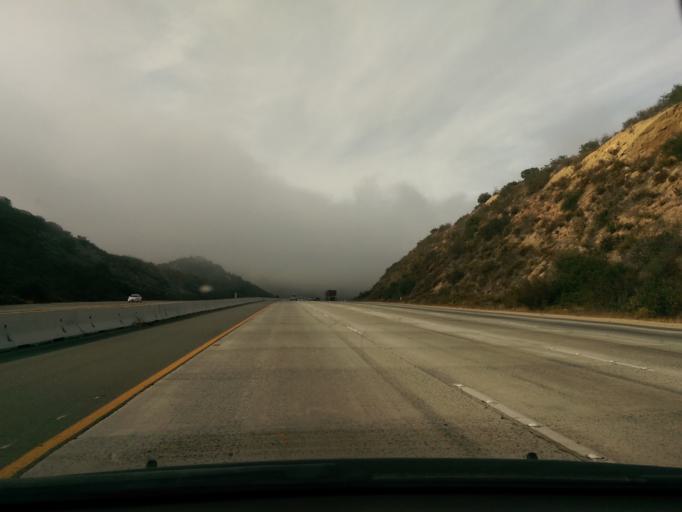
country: US
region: California
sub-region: Riverside County
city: Temecula
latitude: 33.4539
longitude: -117.1356
